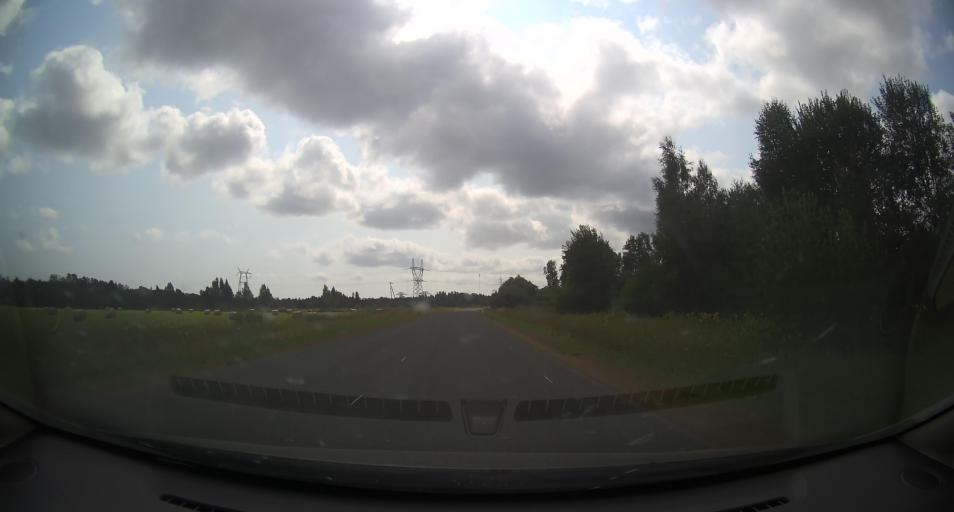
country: EE
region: Paernumaa
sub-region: Audru vald
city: Audru
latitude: 58.4286
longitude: 24.3152
